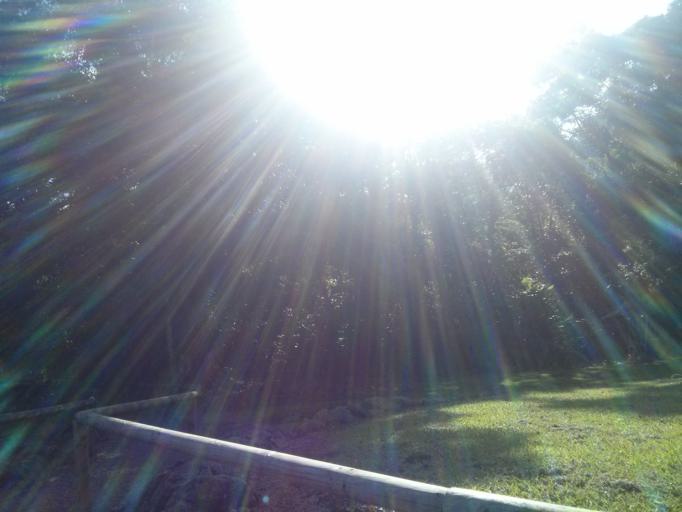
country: CR
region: Cartago
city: Turrialba
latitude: 9.9730
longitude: -83.6910
